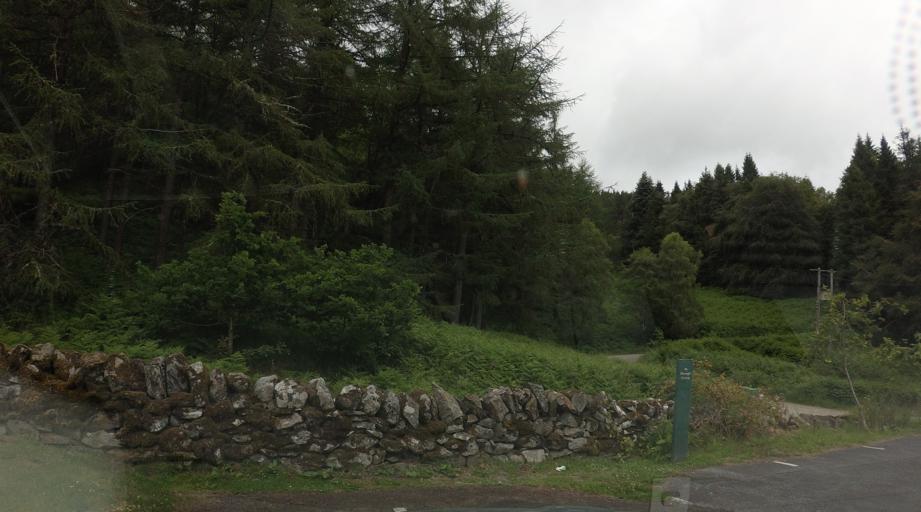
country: GB
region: Scotland
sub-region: Perth and Kinross
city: Aberfeldy
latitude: 56.7171
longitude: -3.8561
